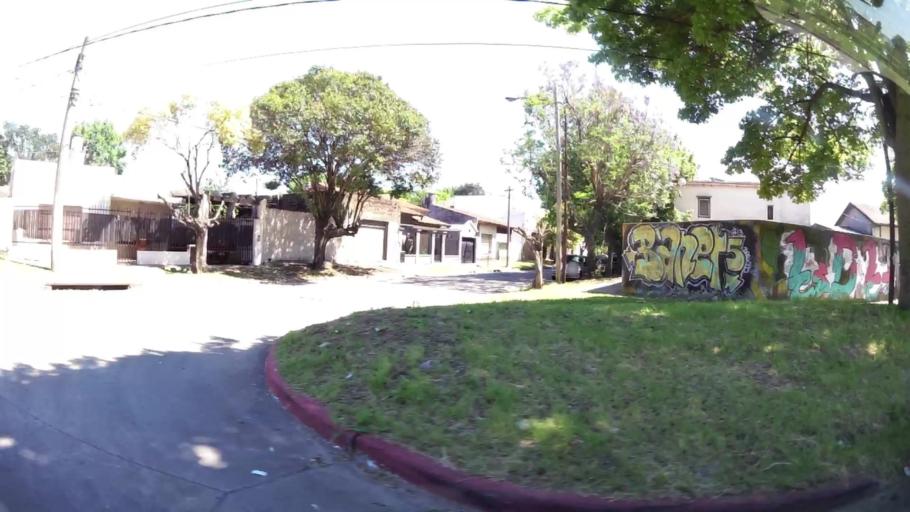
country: AR
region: Buenos Aires
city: Ituzaingo
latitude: -34.6625
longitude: -58.6454
